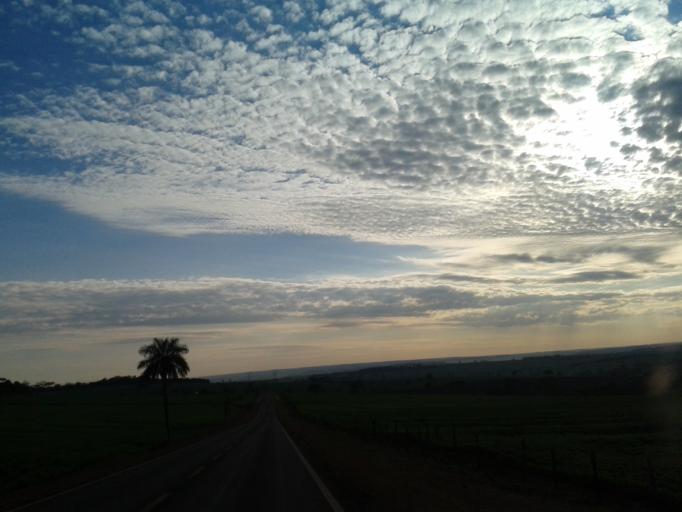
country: BR
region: Minas Gerais
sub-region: Capinopolis
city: Capinopolis
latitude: -18.6923
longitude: -49.4725
